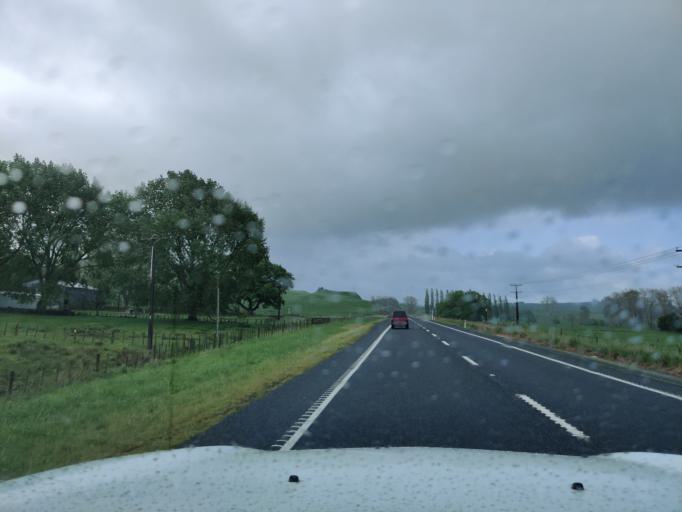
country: NZ
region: Waikato
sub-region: Matamata-Piako District
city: Matamata
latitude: -37.9641
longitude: 175.6884
